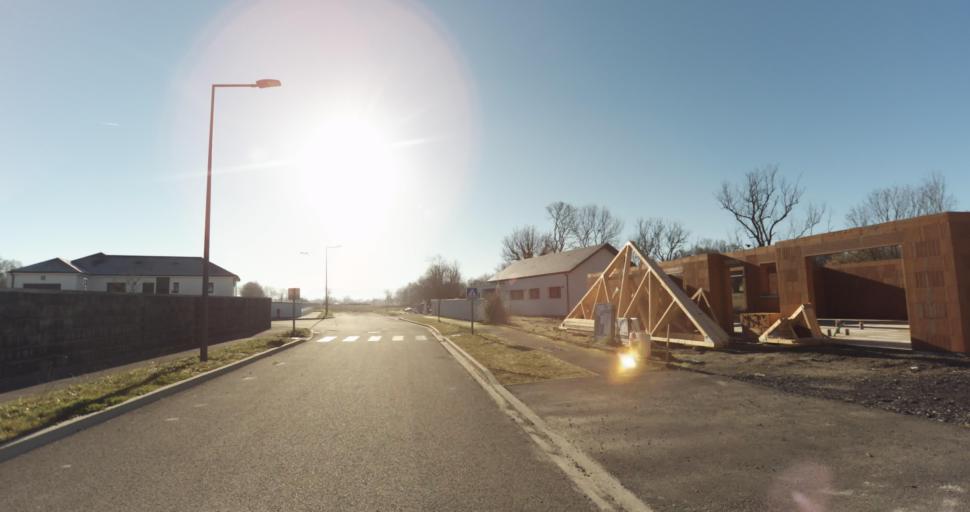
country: FR
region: Aquitaine
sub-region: Departement des Pyrenees-Atlantiques
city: Morlaas
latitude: 43.3397
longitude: -0.2580
